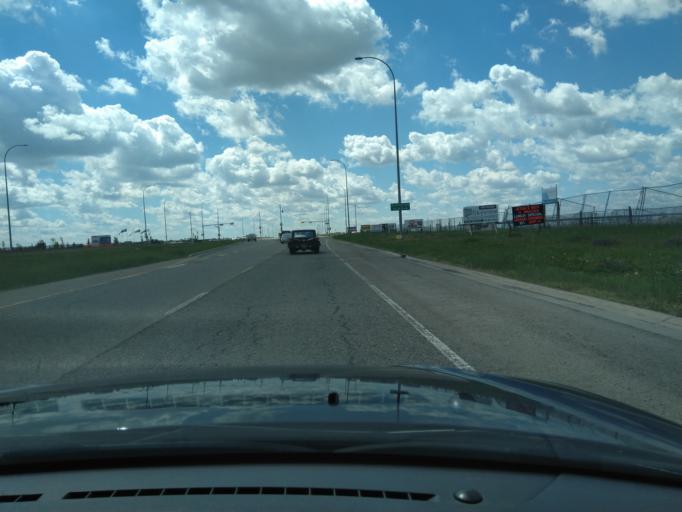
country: CA
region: Alberta
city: Calgary
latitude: 51.1491
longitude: -113.9703
